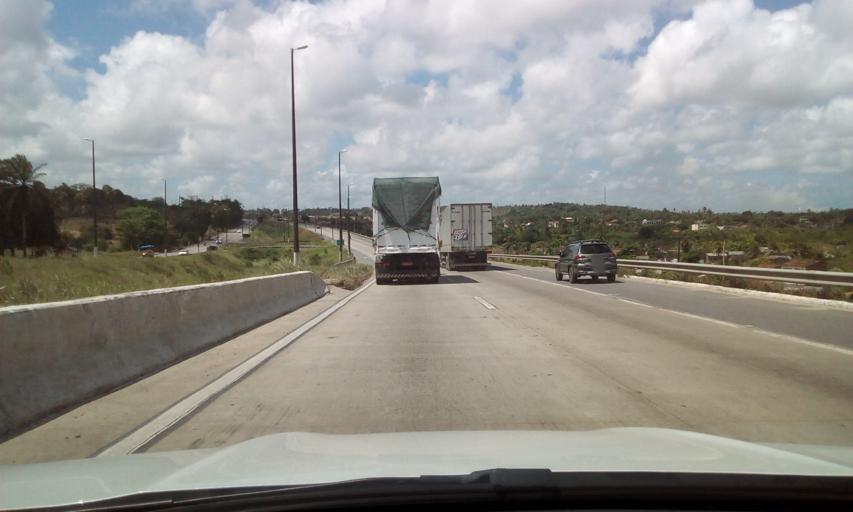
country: BR
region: Pernambuco
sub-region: Igarassu
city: Igarassu
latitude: -7.8182
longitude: -34.9171
